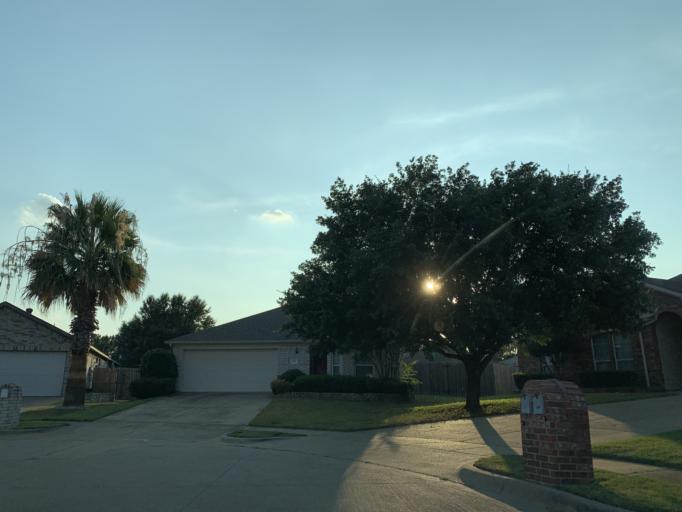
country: US
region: Texas
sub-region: Tarrant County
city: Richland Hills
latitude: 32.7826
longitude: -97.1970
